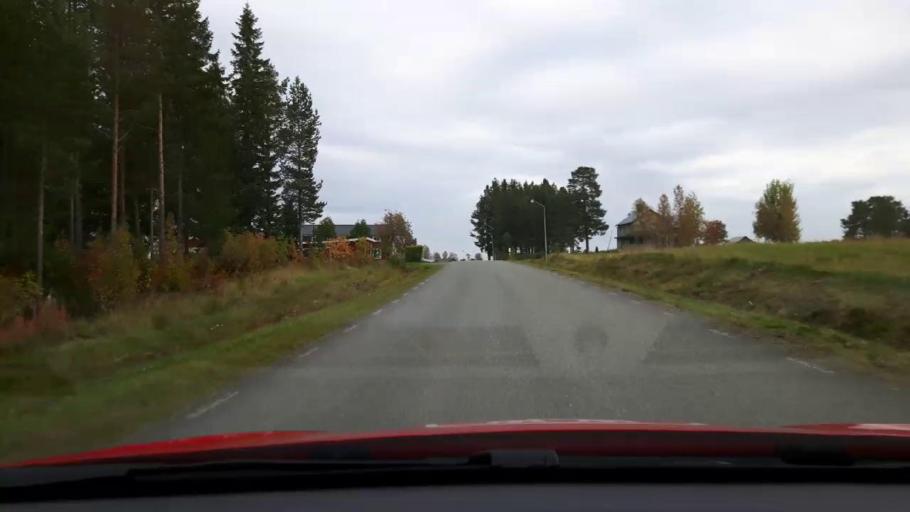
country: SE
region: Jaemtland
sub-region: Krokoms Kommun
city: Krokom
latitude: 63.2360
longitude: 14.1173
